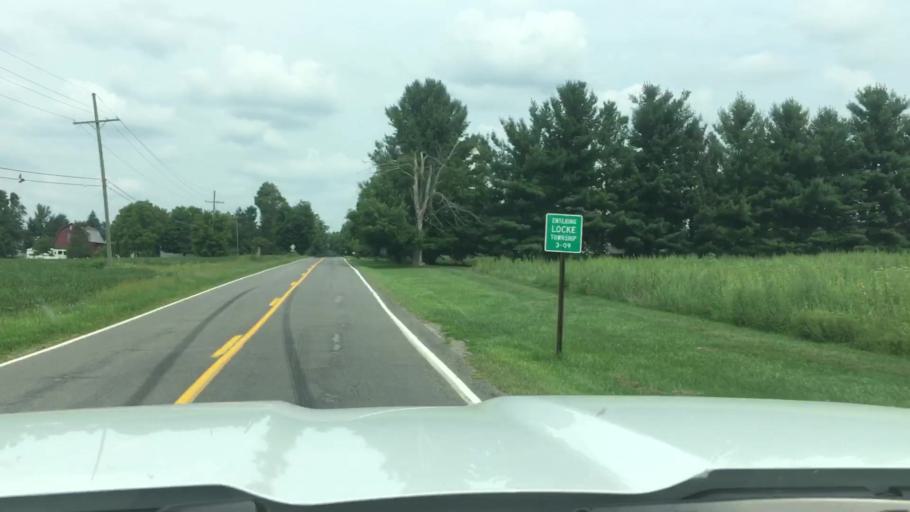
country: US
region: Michigan
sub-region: Ingham County
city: Webberville
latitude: 42.6858
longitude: -84.1899
